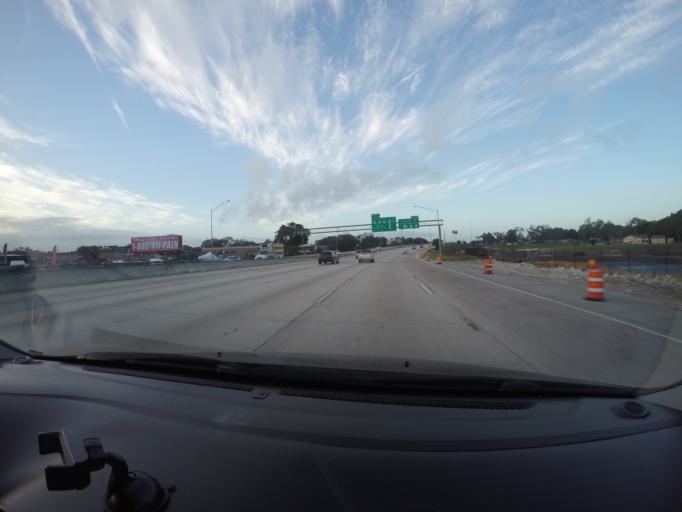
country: US
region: Florida
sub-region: Orange County
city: Holden Heights
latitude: 28.5170
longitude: -81.3875
